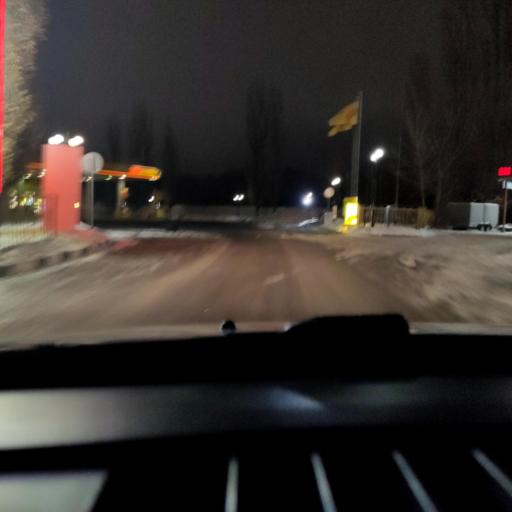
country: RU
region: Voronezj
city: Voronezh
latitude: 51.7041
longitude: 39.2759
